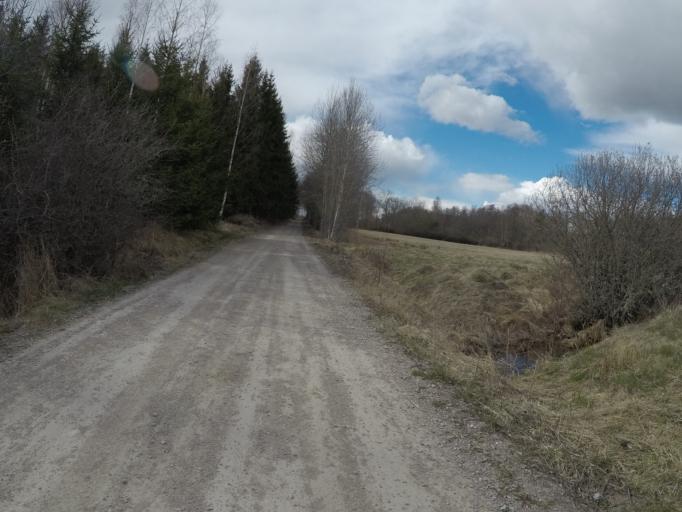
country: SE
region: Soedermanland
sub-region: Eskilstuna Kommun
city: Kvicksund
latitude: 59.4724
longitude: 16.3025
